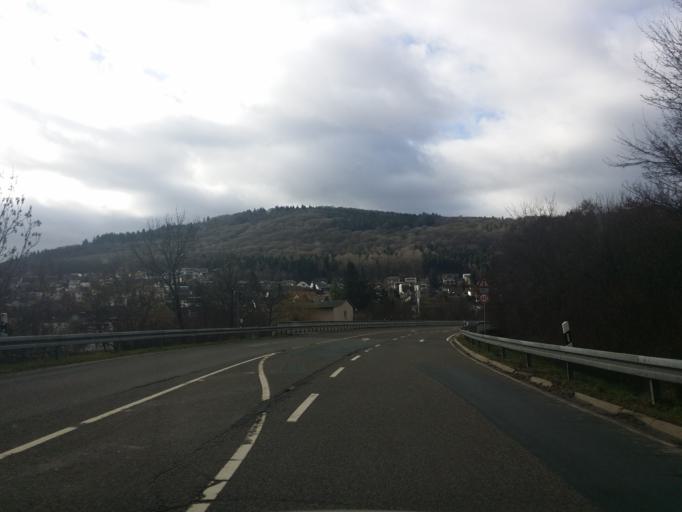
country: DE
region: Hesse
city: Kelkheim (Taunus)
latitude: 50.1519
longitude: 8.4245
